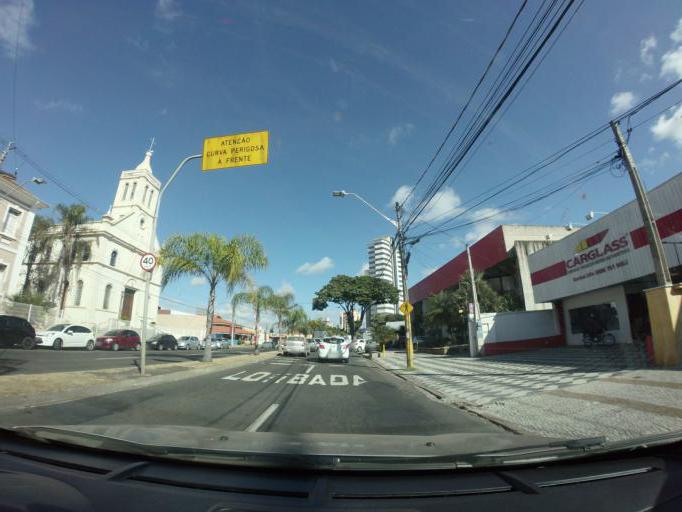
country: BR
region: Sao Paulo
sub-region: Piracicaba
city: Piracicaba
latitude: -22.7381
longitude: -47.6418
